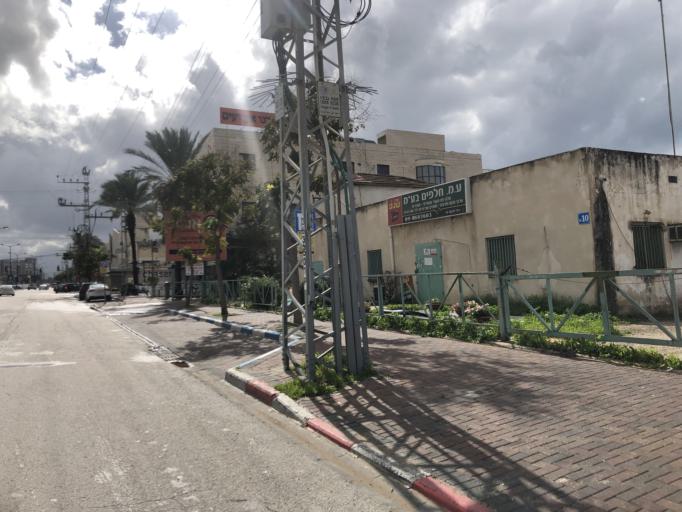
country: IL
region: Central District
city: Bet Yizhaq
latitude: 32.3221
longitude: 34.8744
